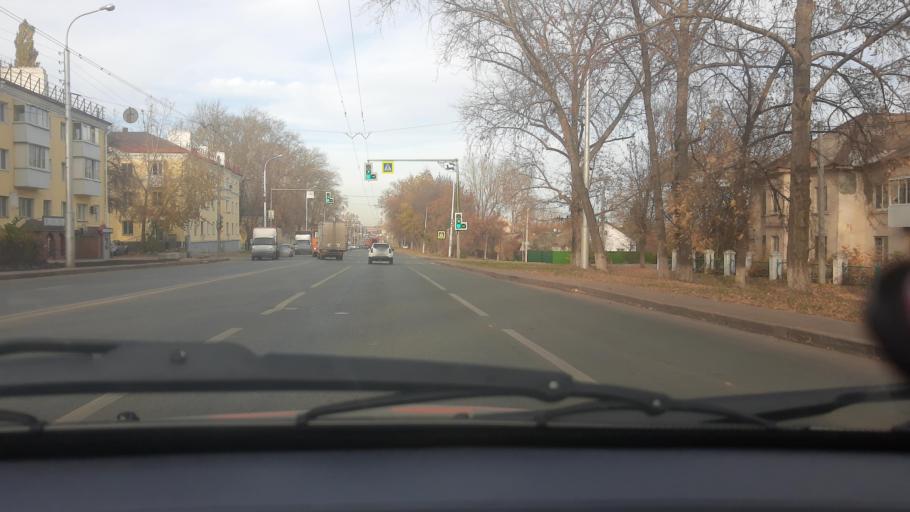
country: RU
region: Bashkortostan
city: Ufa
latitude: 54.8222
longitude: 56.1102
